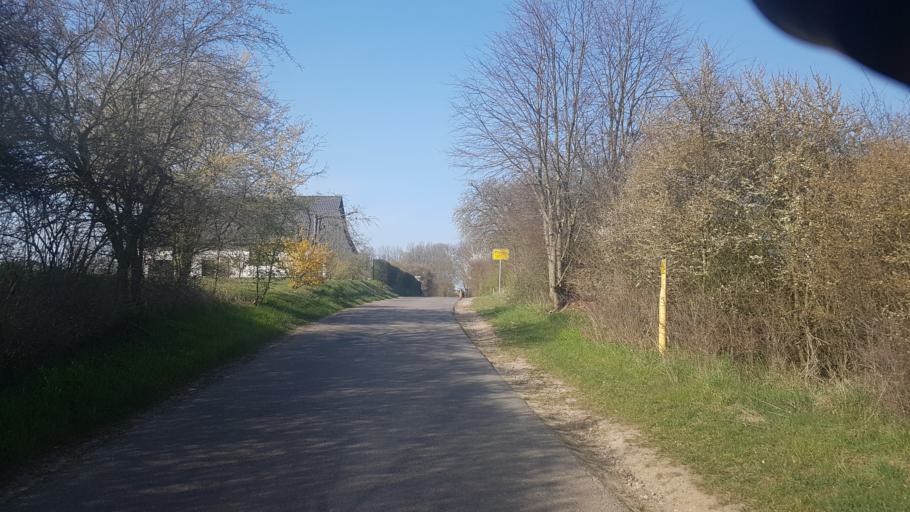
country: DE
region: Brandenburg
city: Gerswalde
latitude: 53.2035
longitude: 13.7824
